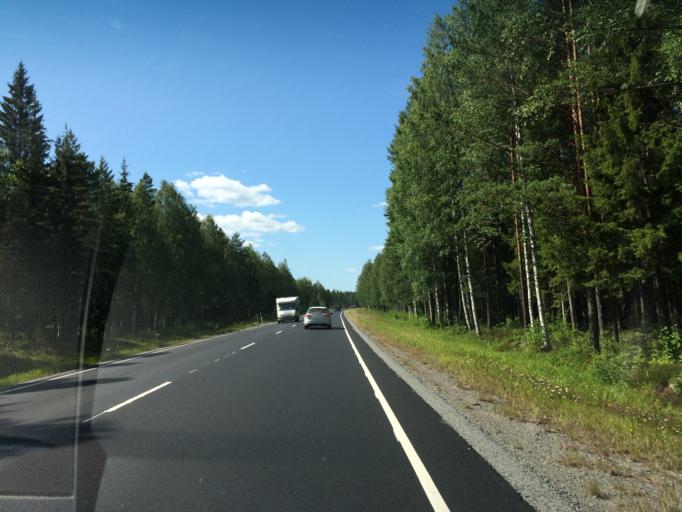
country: FI
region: Pirkanmaa
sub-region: Lounais-Pirkanmaa
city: Kiikoinen
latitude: 61.4731
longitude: 22.5195
